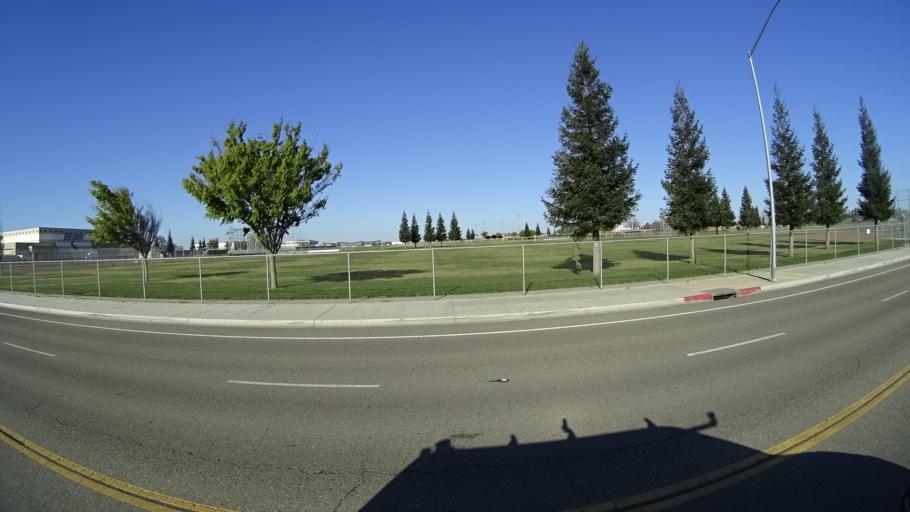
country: US
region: California
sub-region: Fresno County
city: West Park
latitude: 36.7966
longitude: -119.9073
